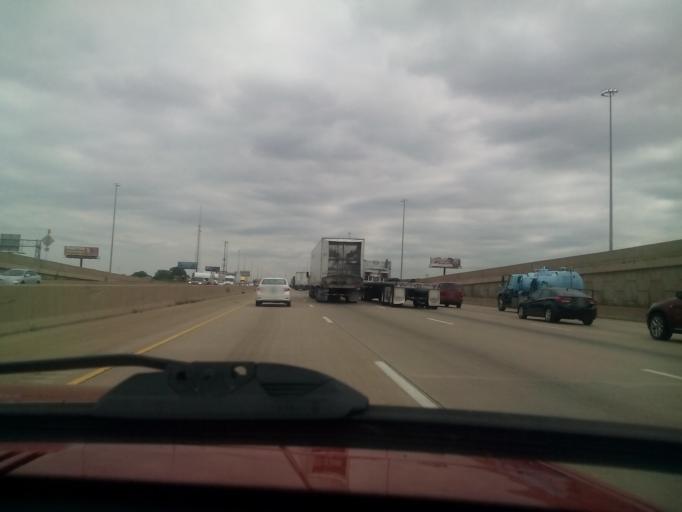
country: US
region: Illinois
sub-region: Cook County
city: Lansing
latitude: 41.5777
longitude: -87.5576
